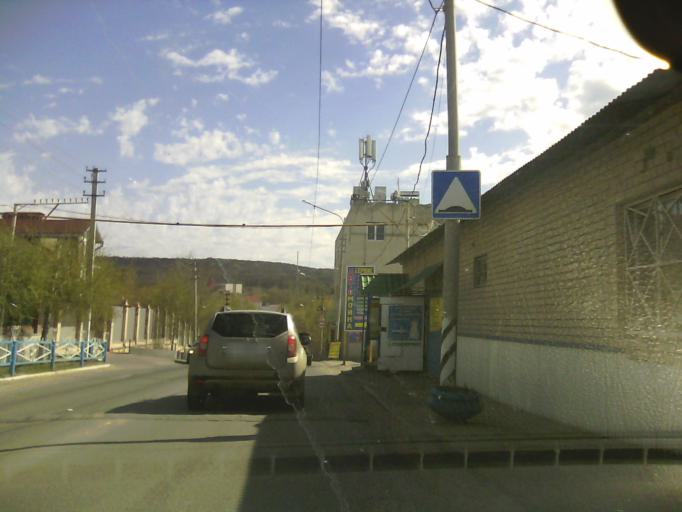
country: RU
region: Saratov
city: Sokolovyy
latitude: 51.5772
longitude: 45.8995
